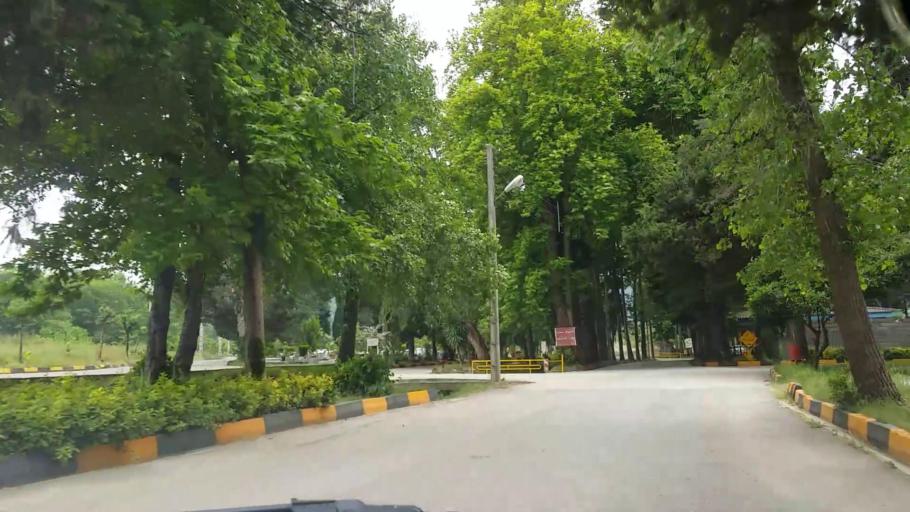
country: IR
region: Mazandaran
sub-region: Nowshahr
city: Nowshahr
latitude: 36.6282
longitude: 51.5027
